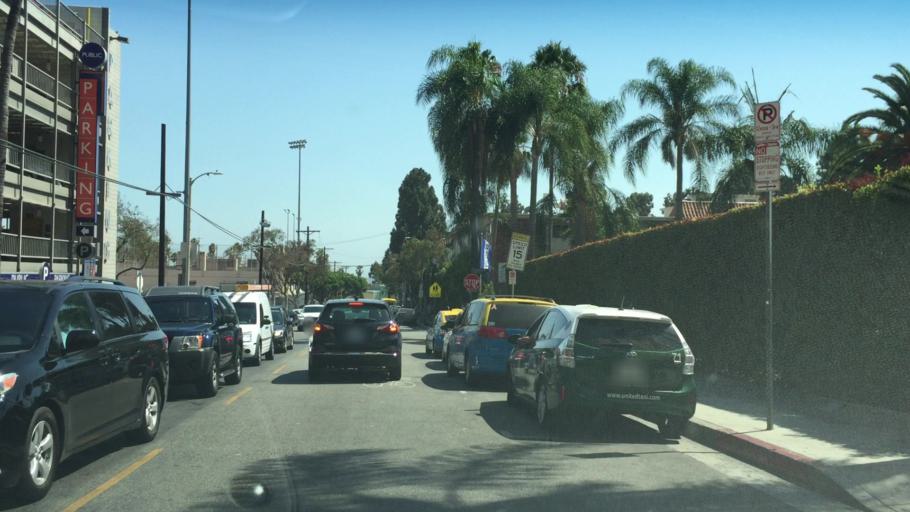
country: US
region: California
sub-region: Los Angeles County
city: Hollywood
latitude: 34.1009
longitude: -118.3415
